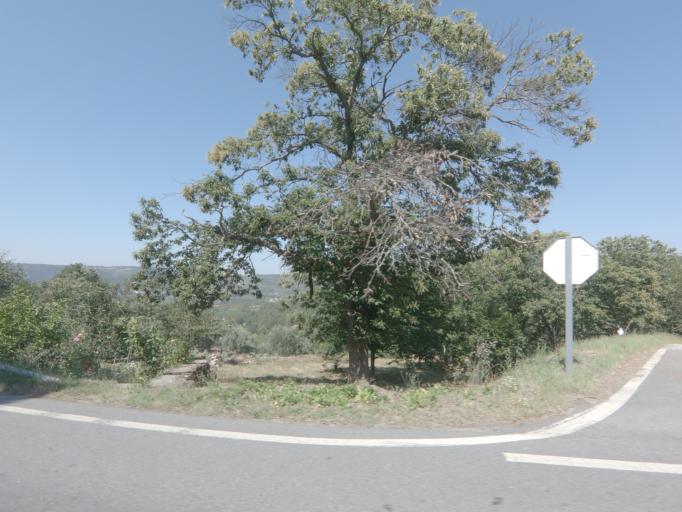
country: PT
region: Viseu
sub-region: Tarouca
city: Tarouca
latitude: 41.0368
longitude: -7.7327
